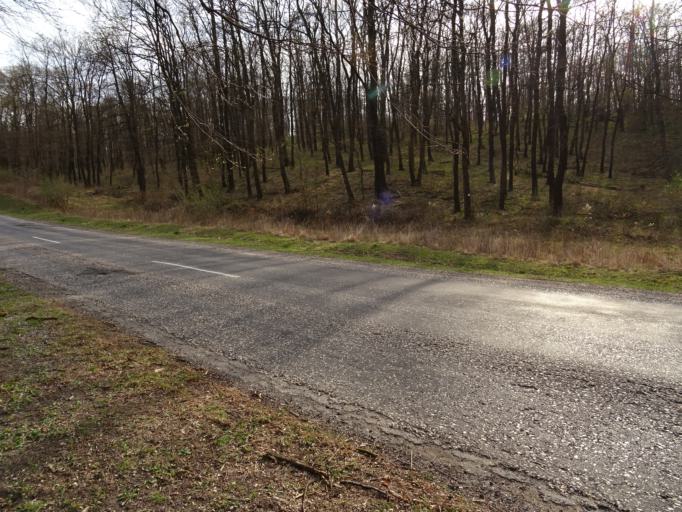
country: HU
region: Fejer
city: Pazmand
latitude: 47.2704
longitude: 18.5968
